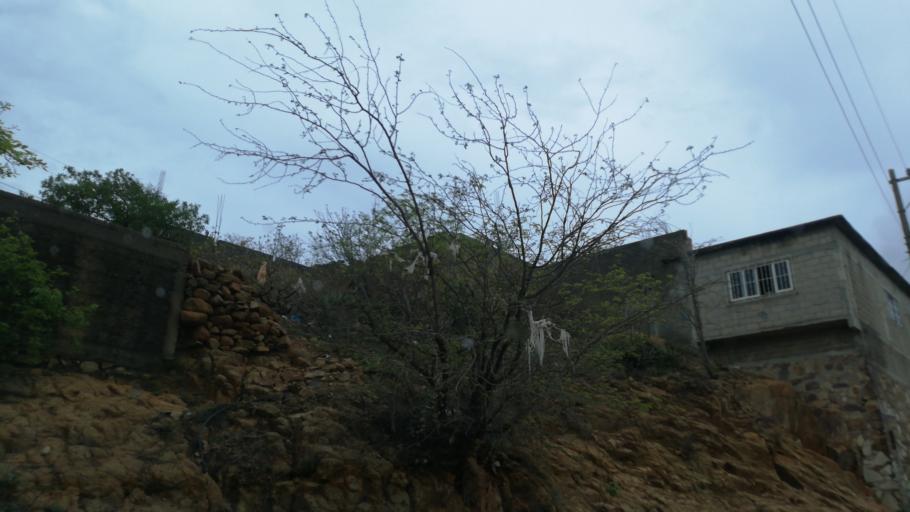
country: MX
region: Oaxaca
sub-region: Salina Cruz
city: Salina Cruz
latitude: 16.1802
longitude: -95.1832
